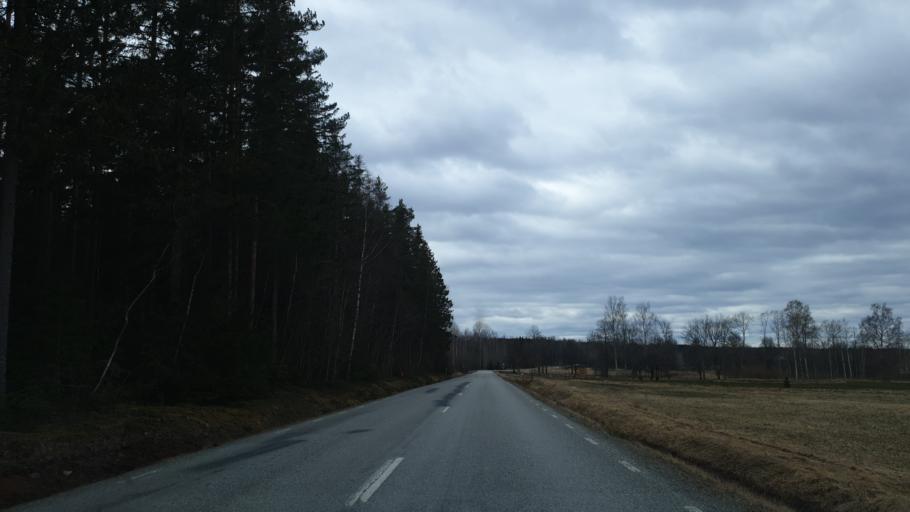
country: SE
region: OErebro
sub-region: Nora Kommun
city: As
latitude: 59.5813
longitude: 14.9740
